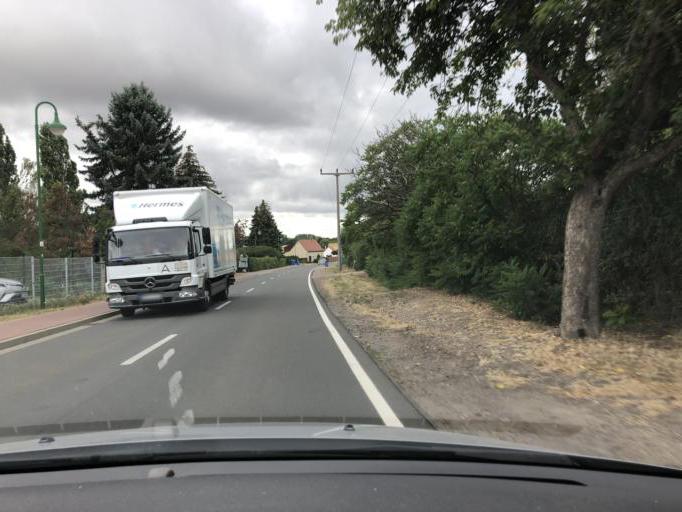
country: DE
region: Saxony-Anhalt
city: Ermlitz
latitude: 51.3886
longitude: 12.1500
